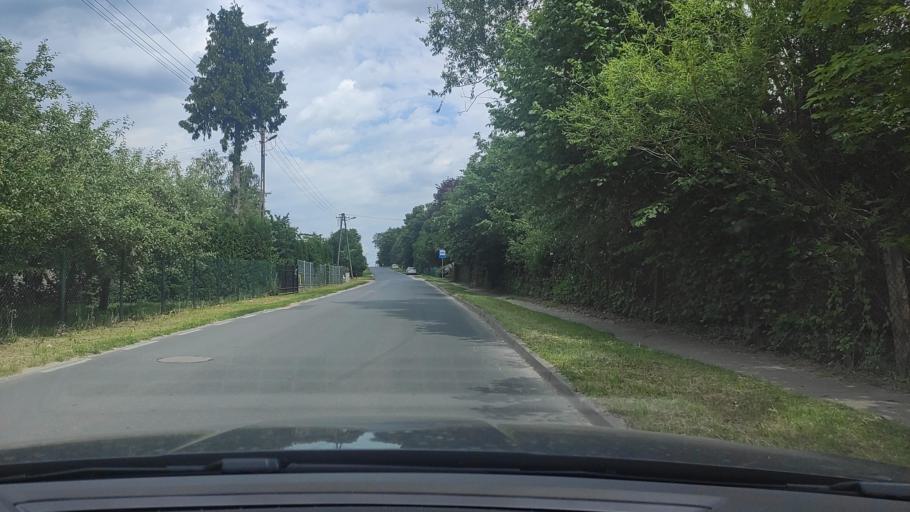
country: PL
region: Greater Poland Voivodeship
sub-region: Powiat poznanski
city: Kostrzyn
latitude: 52.4783
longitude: 17.1861
